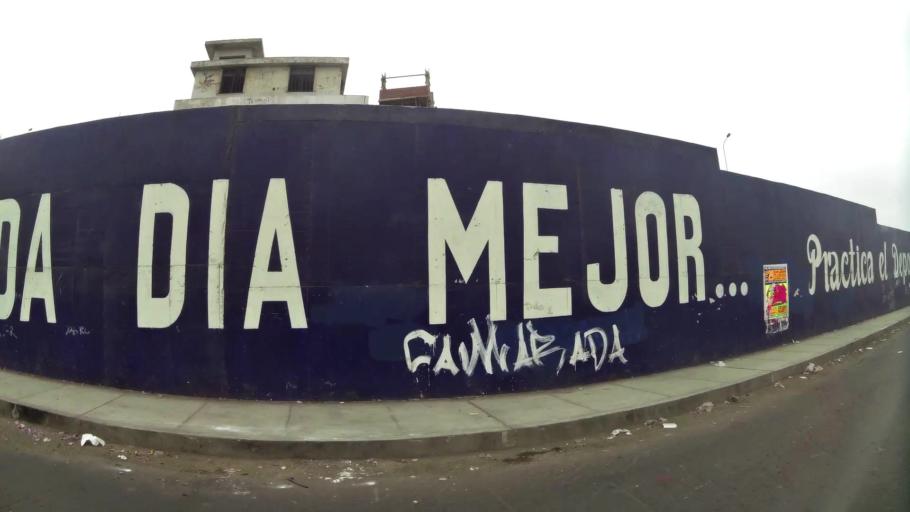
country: PE
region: Lima
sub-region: Lima
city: Surco
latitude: -12.1891
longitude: -76.9912
